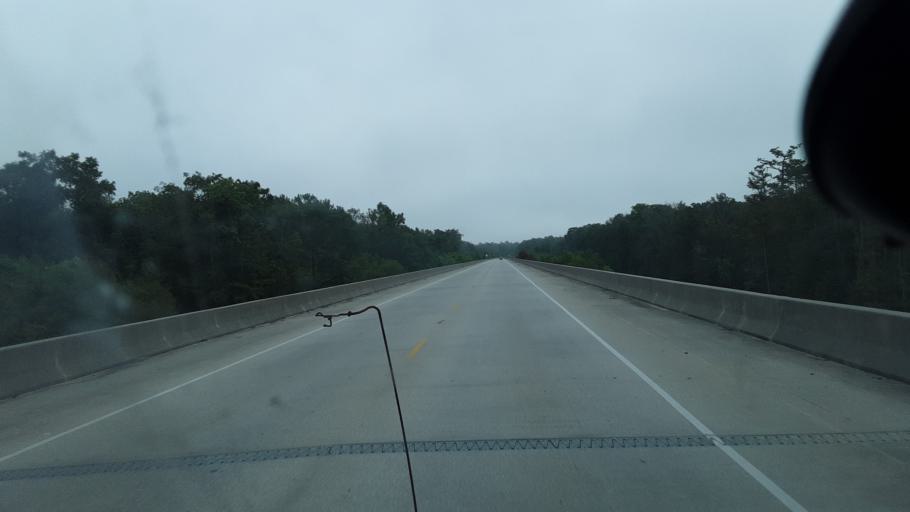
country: US
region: South Carolina
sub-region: Florence County
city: Johnsonville
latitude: 33.9074
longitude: -79.4303
